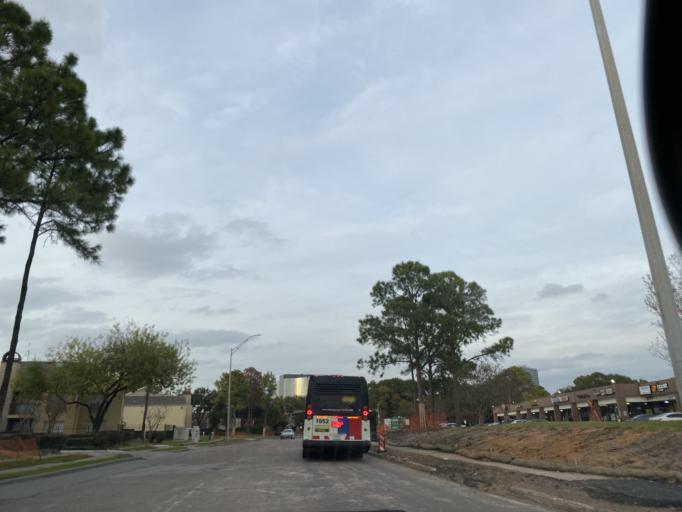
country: US
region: Texas
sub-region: Harris County
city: Bunker Hill Village
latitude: 29.7312
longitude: -95.5680
